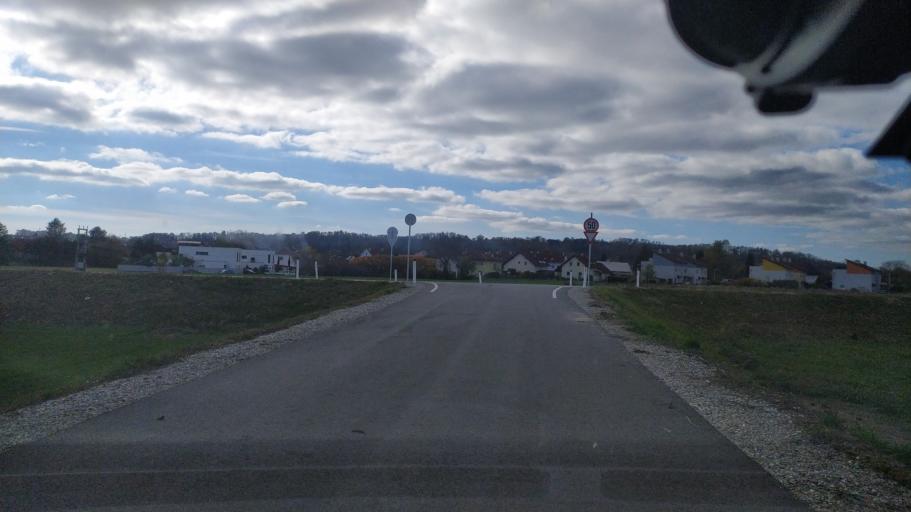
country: AT
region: Upper Austria
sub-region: Politischer Bezirk Urfahr-Umgebung
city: Steyregg
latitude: 48.2539
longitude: 14.3748
